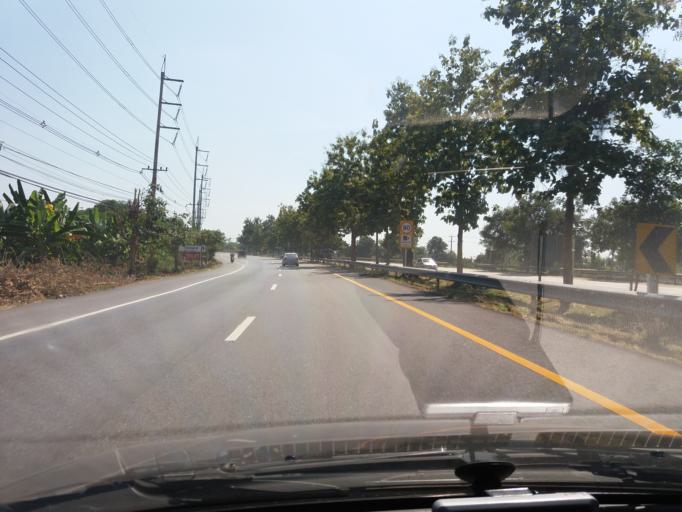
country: TH
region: Chai Nat
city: Sankhaburi
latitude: 15.1034
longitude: 100.1363
